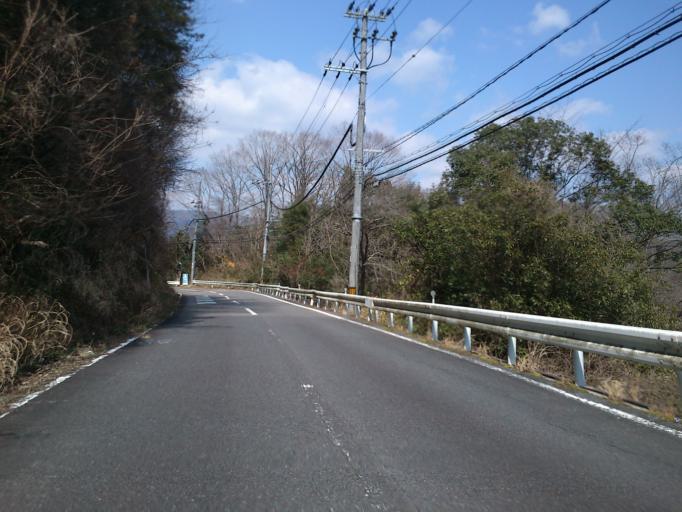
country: JP
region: Mie
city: Ueno-ebisumachi
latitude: 34.7474
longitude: 136.0116
